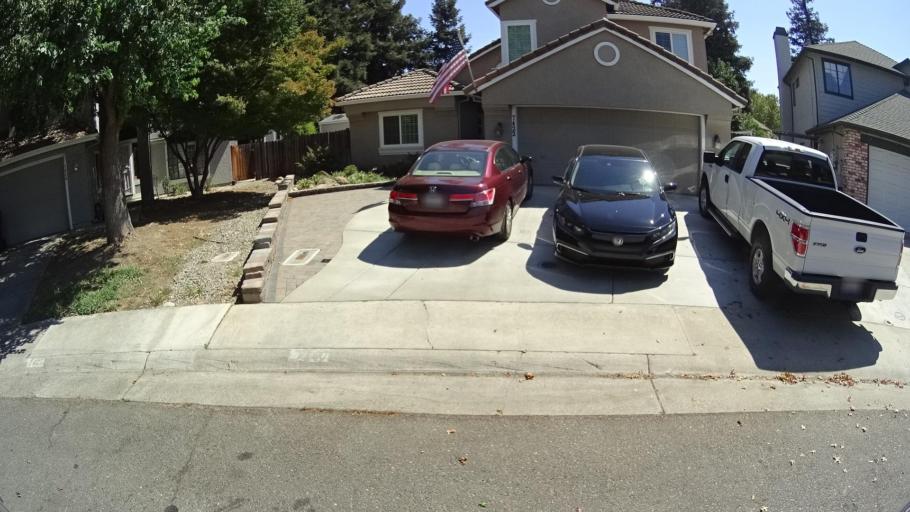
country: US
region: California
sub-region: Sacramento County
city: Laguna
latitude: 38.4172
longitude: -121.4161
